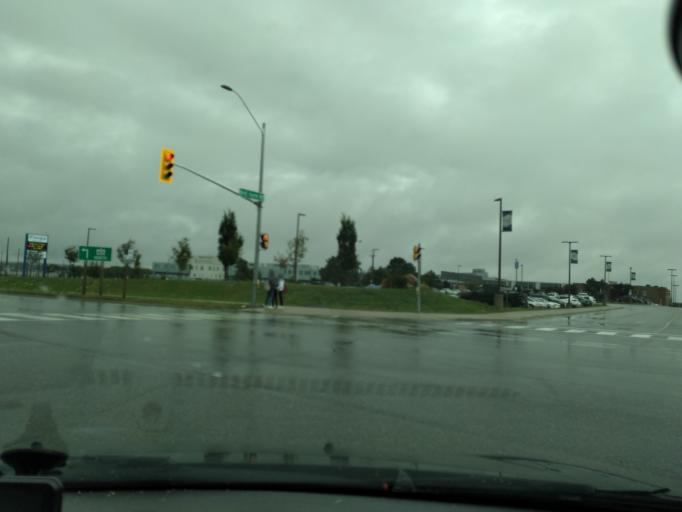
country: CA
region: Ontario
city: Barrie
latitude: 44.4109
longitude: -79.6737
